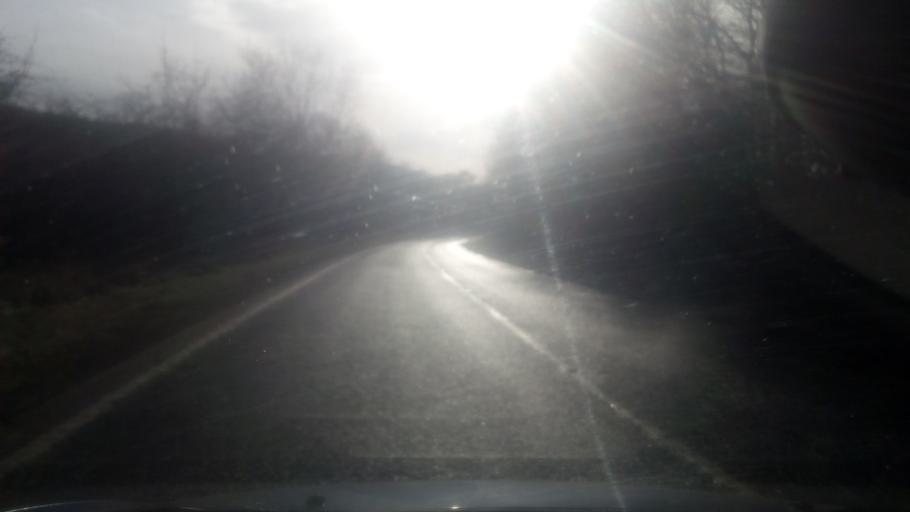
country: GB
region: Scotland
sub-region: The Scottish Borders
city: Jedburgh
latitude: 55.4173
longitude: -2.5099
